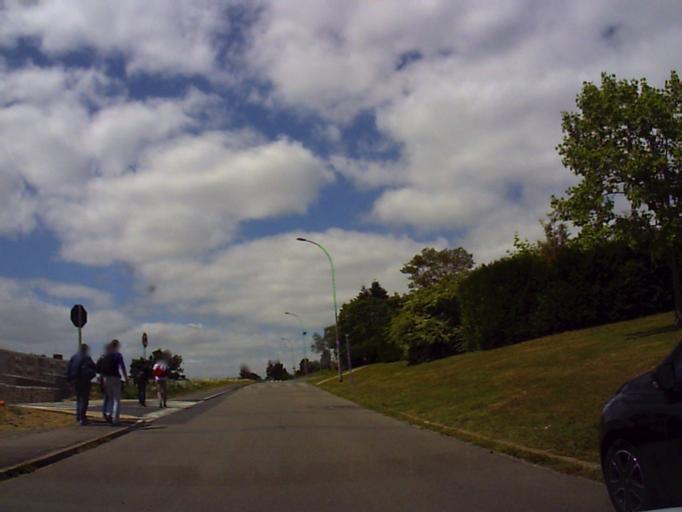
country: FR
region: Brittany
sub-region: Departement d'Ille-et-Vilaine
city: Rennes
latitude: 48.1231
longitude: -1.6407
